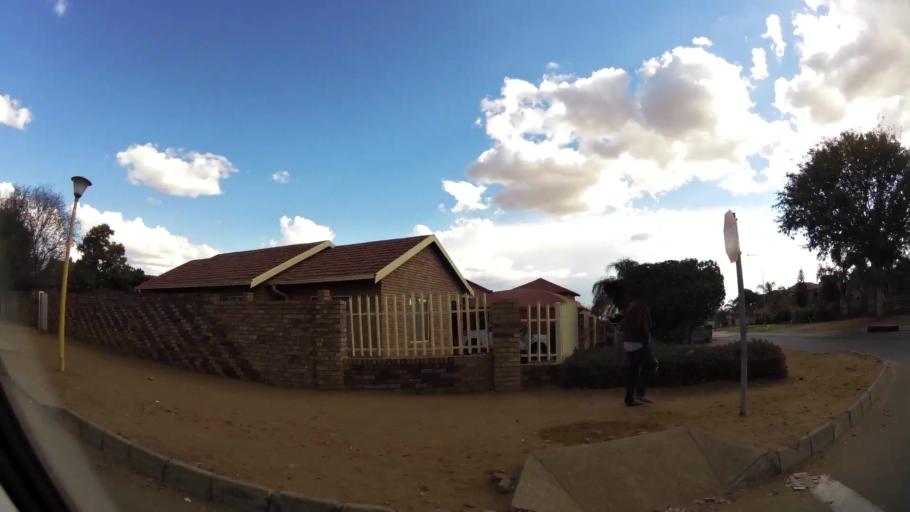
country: ZA
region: Limpopo
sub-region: Capricorn District Municipality
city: Polokwane
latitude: -23.9122
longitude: 29.4994
